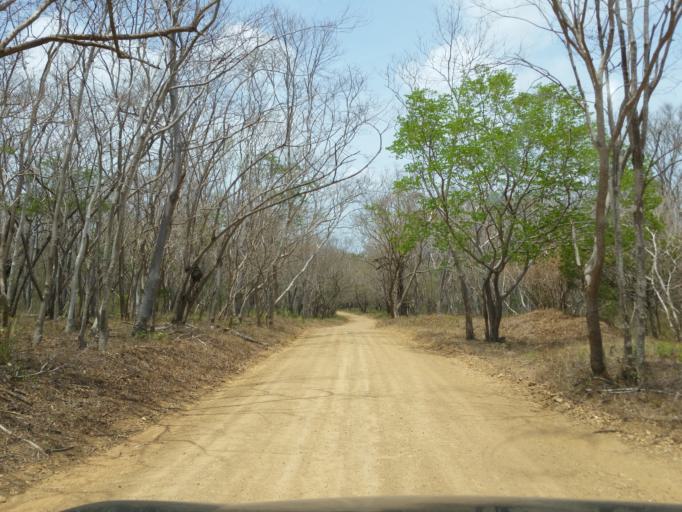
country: NI
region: Rivas
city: Tola
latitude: 11.4202
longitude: -86.0606
